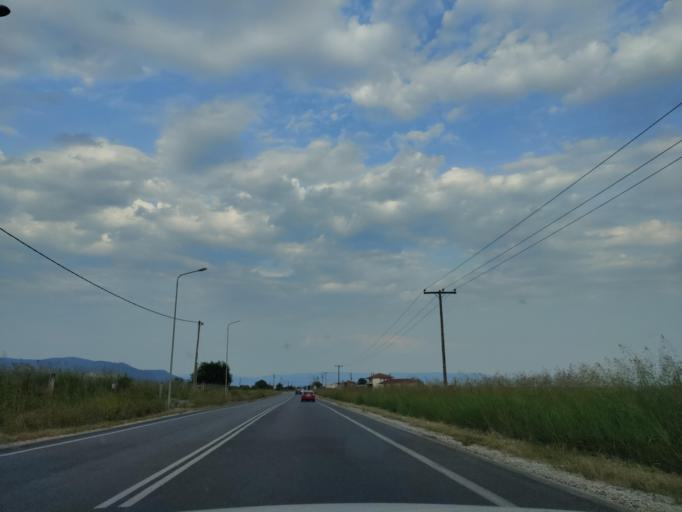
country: GR
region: East Macedonia and Thrace
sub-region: Nomos Dramas
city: Xiropotamos
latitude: 41.1614
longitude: 24.0809
